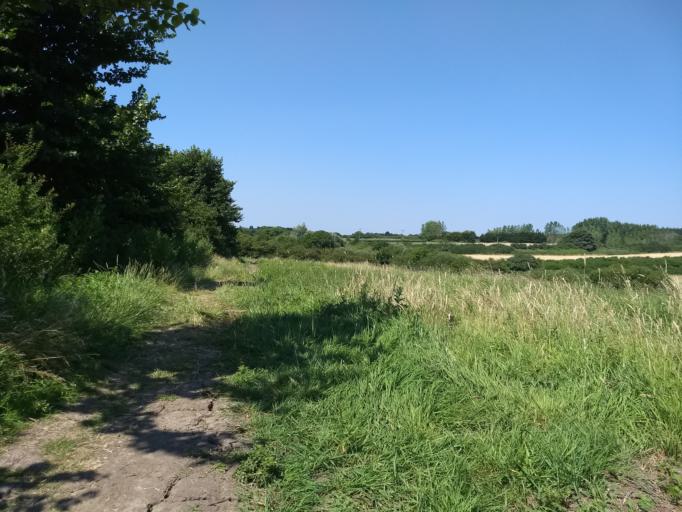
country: GB
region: England
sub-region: Isle of Wight
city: Newport
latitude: 50.7012
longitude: -1.3091
